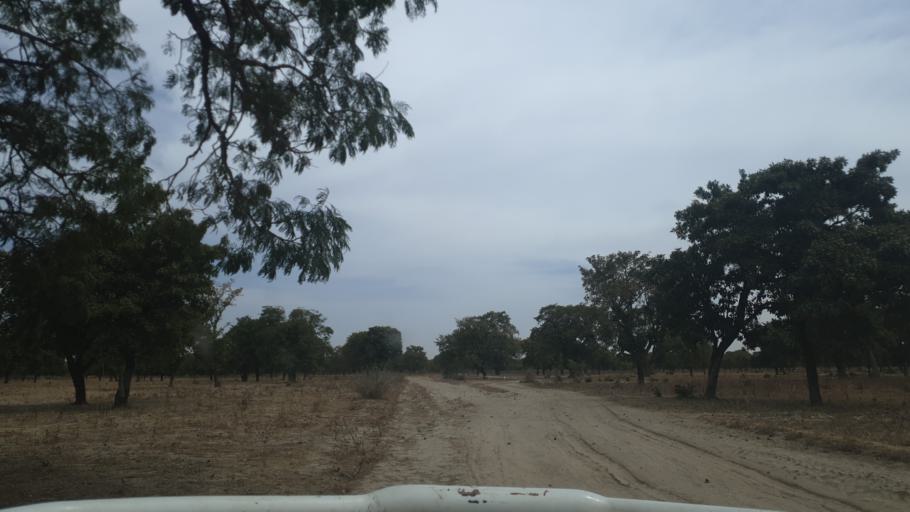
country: ML
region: Sikasso
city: Yorosso
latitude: 12.2385
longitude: -4.7371
